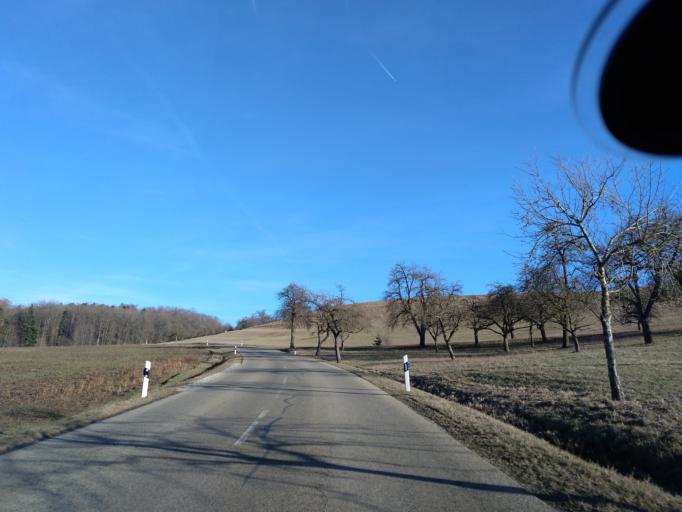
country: DE
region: Baden-Wuerttemberg
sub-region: Regierungsbezirk Stuttgart
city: Buhlertann
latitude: 49.0841
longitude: 9.9605
